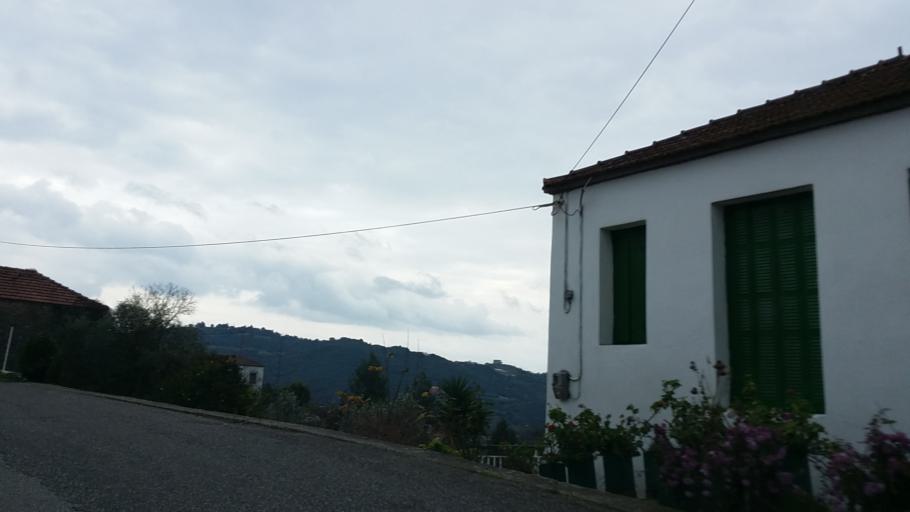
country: GR
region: West Greece
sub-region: Nomos Aitolias kai Akarnanias
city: Fitiai
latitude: 38.7085
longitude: 21.1698
